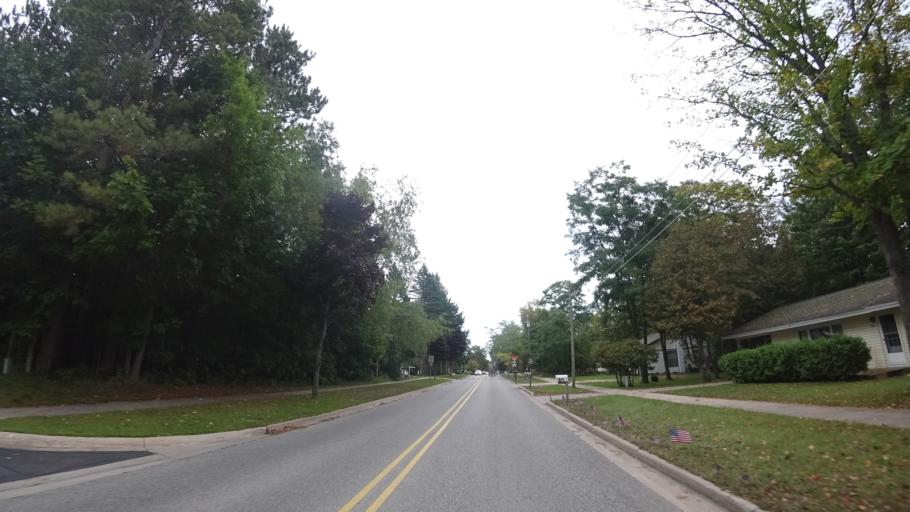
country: US
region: Michigan
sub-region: Emmet County
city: Harbor Springs
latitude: 45.4354
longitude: -84.9843
